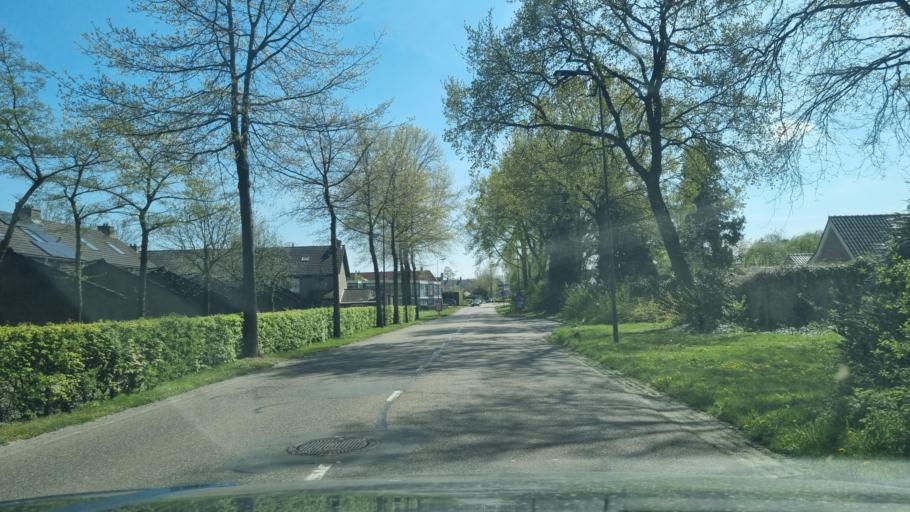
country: NL
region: North Brabant
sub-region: Gemeente 's-Hertogenbosch
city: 's-Hertogenbosch
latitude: 51.7216
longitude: 5.3636
